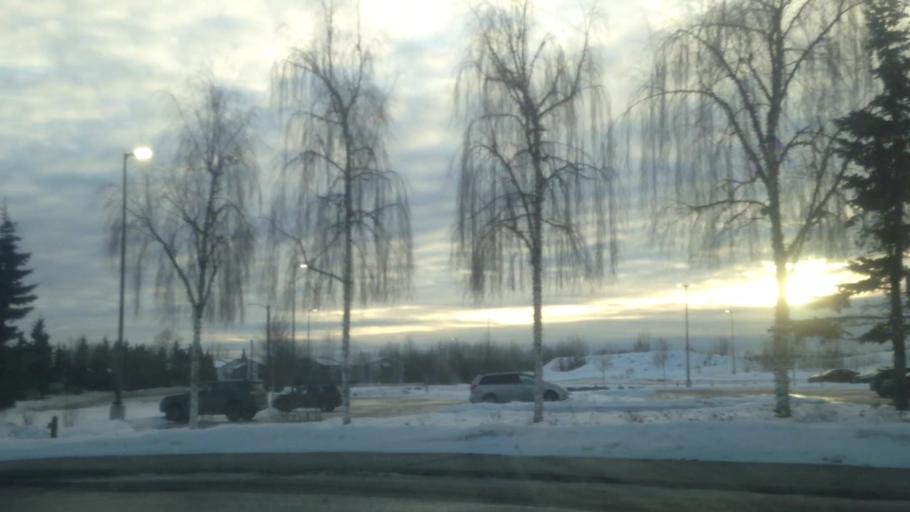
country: US
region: Alaska
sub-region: Anchorage Municipality
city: Anchorage
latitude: 61.2099
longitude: -149.8314
